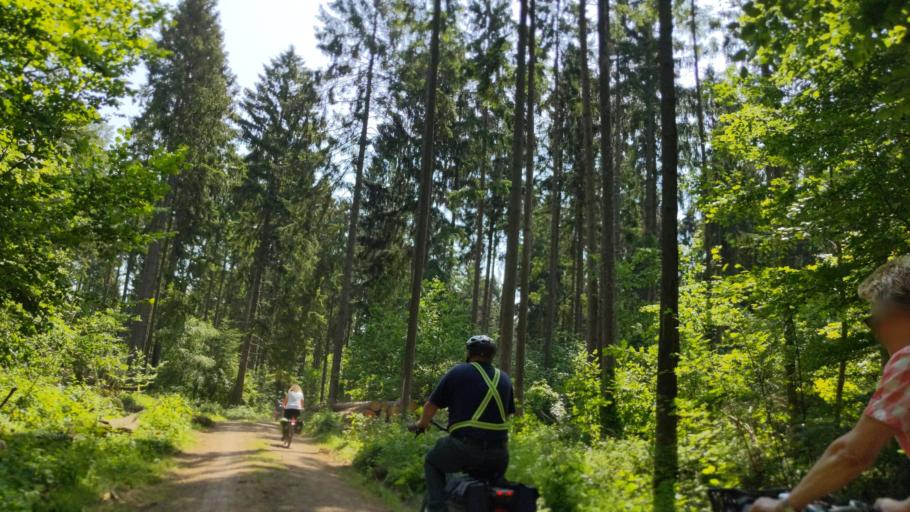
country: DE
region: Schleswig-Holstein
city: Albsfelde
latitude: 53.6762
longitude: 10.7030
